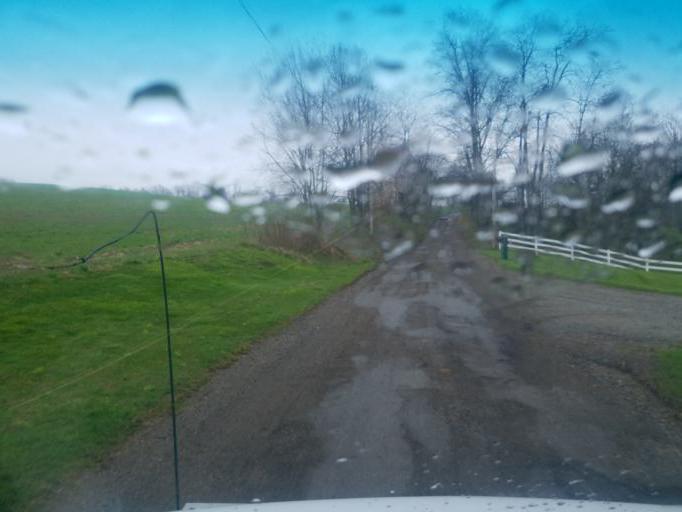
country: US
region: Ohio
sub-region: Holmes County
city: Millersburg
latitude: 40.6428
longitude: -81.8794
